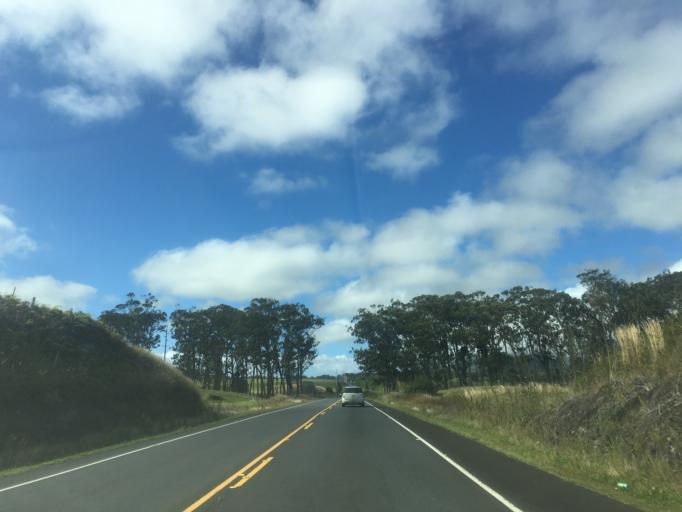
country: US
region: Hawaii
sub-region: Hawaii County
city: Waimea
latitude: 20.0496
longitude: -155.5706
